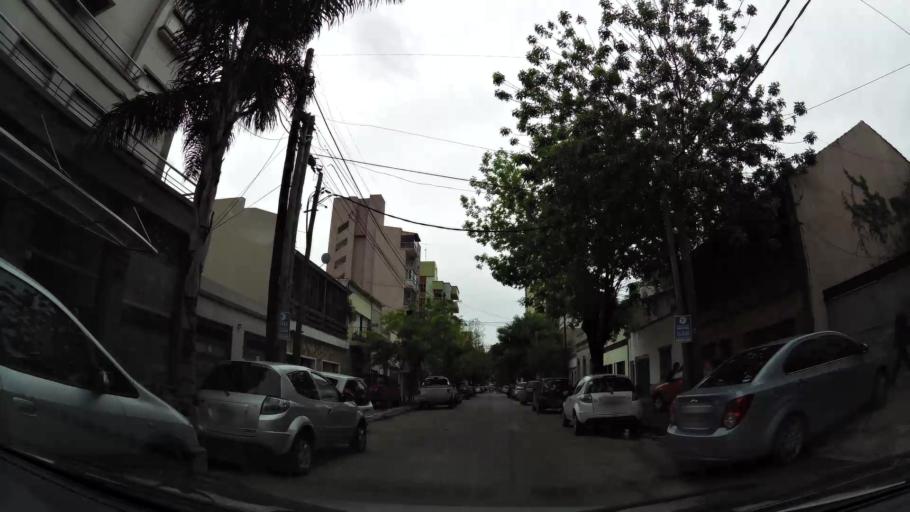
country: AR
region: Buenos Aires
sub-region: Partido de Lanus
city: Lanus
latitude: -34.7074
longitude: -58.3853
